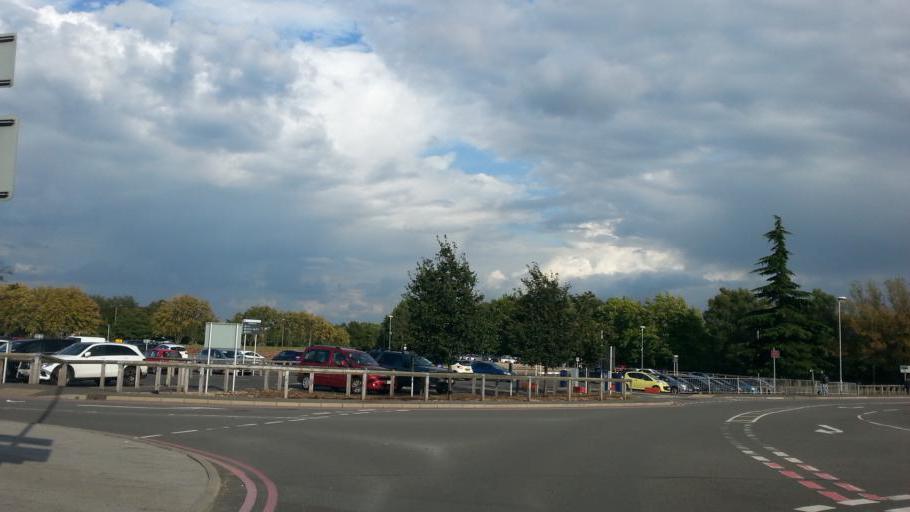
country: GB
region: England
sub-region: Nottinghamshire
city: Sutton in Ashfield
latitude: 53.1345
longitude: -1.2329
